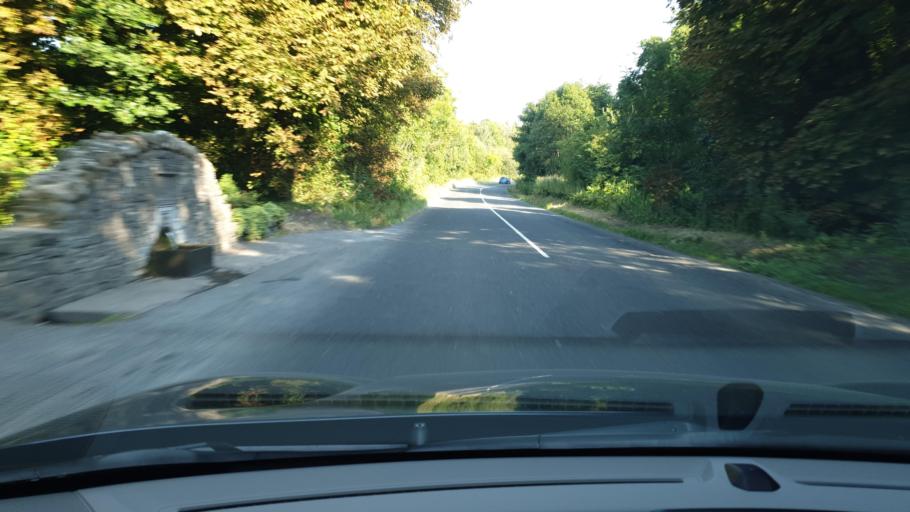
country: IE
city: Kentstown
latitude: 53.6255
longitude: -6.5236
